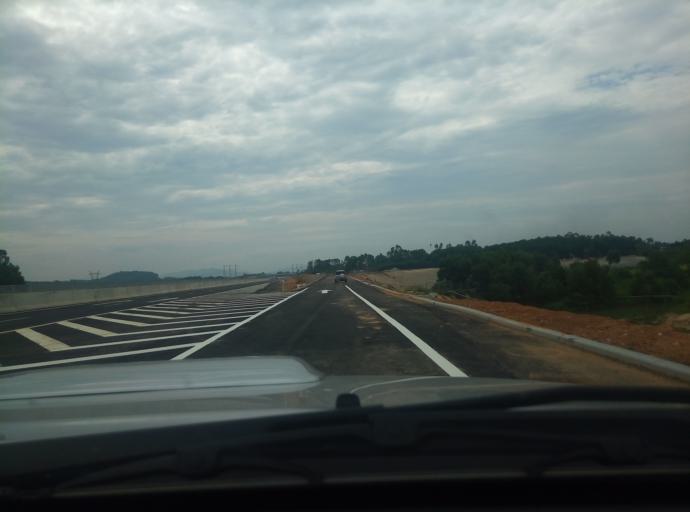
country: VN
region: Quang Nam
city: Tam Ky
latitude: 15.5280
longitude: 108.4802
